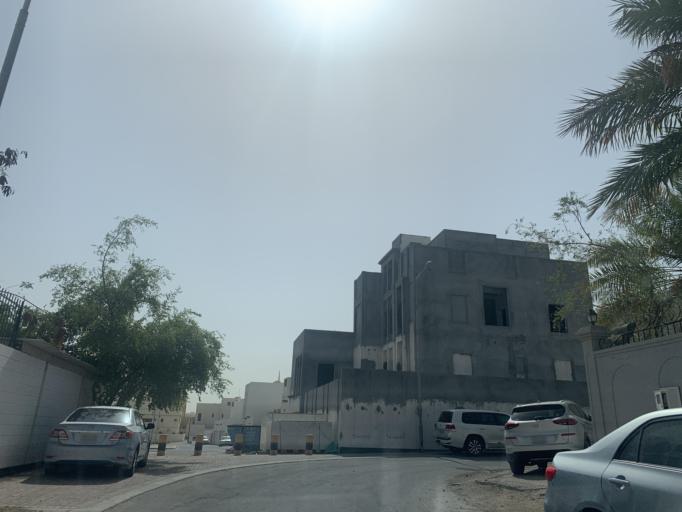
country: BH
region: Northern
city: Madinat `Isa
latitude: 26.1509
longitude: 50.5323
